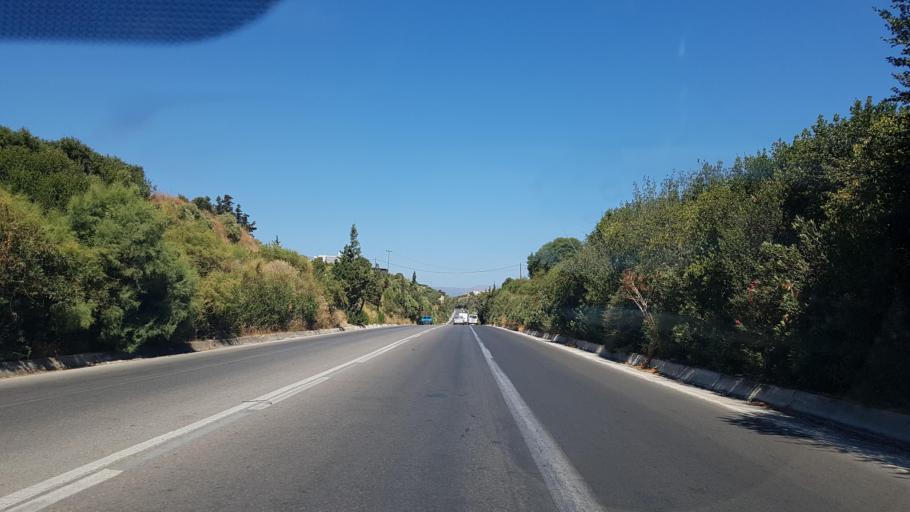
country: GR
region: Crete
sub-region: Nomos Chanias
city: Agia Marina
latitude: 35.5093
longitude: 23.9334
